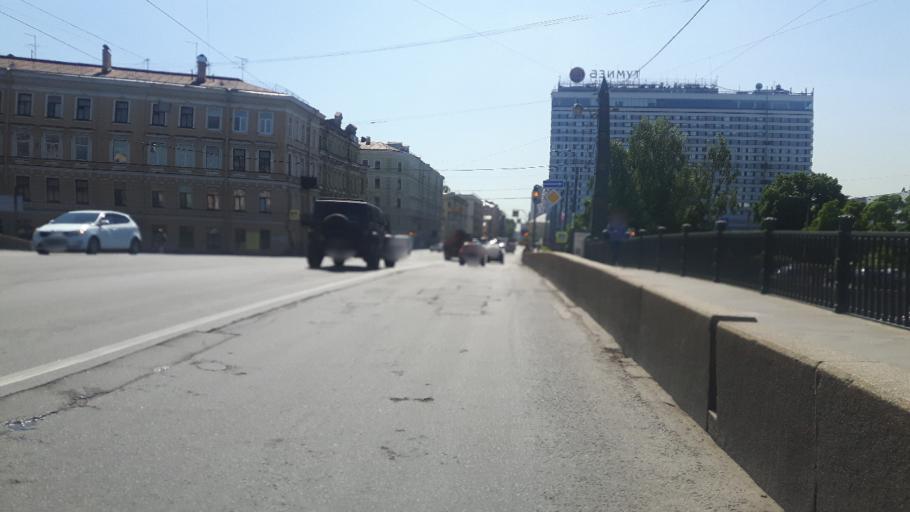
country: RU
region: St.-Petersburg
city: Admiralteisky
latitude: 59.9171
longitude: 30.2971
